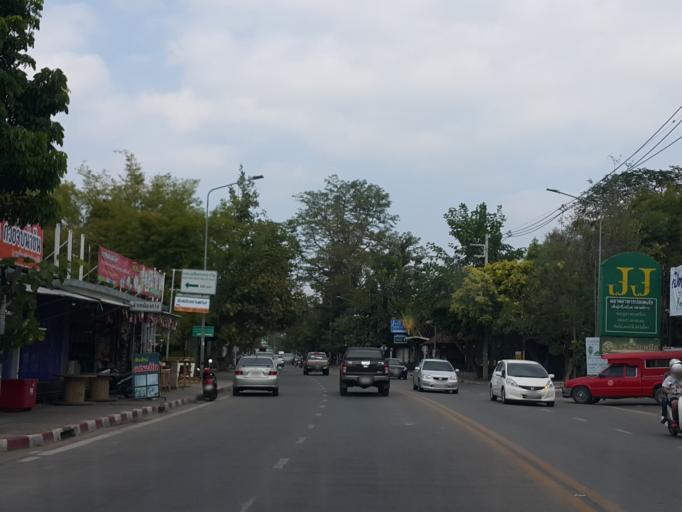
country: TH
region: Chiang Mai
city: Chiang Mai
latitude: 18.8059
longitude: 98.9951
